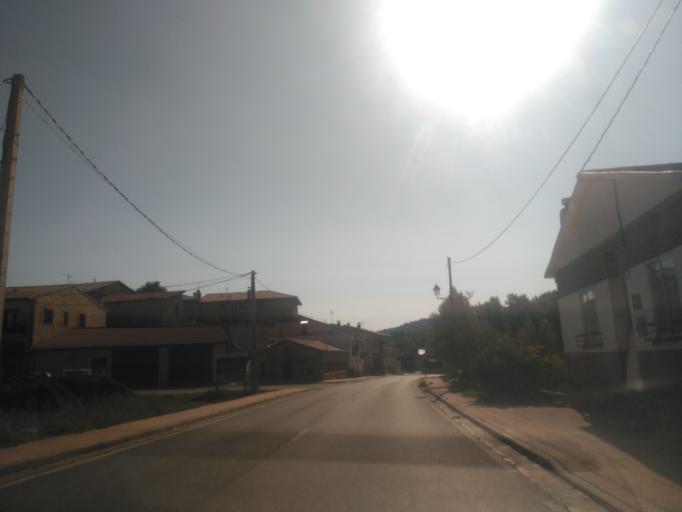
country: ES
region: Castille and Leon
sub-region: Provincia de Soria
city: Casarejos
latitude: 41.7959
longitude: -3.0326
